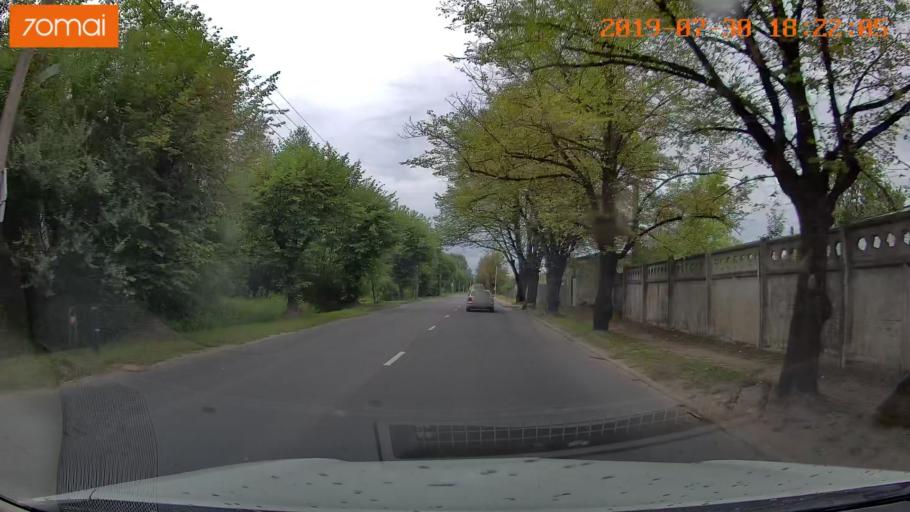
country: LT
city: Skaidiskes
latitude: 54.6948
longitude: 25.4425
